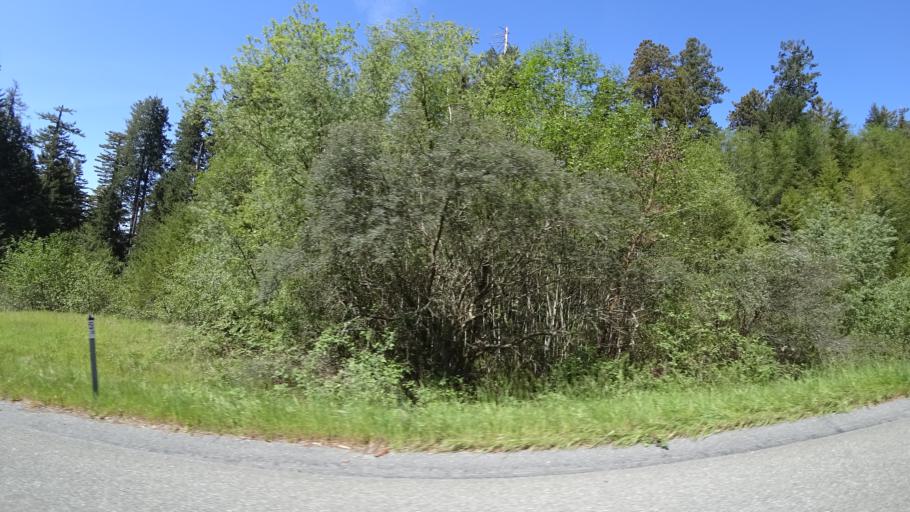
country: US
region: California
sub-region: Humboldt County
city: Westhaven-Moonstone
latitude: 41.3820
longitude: -123.9950
